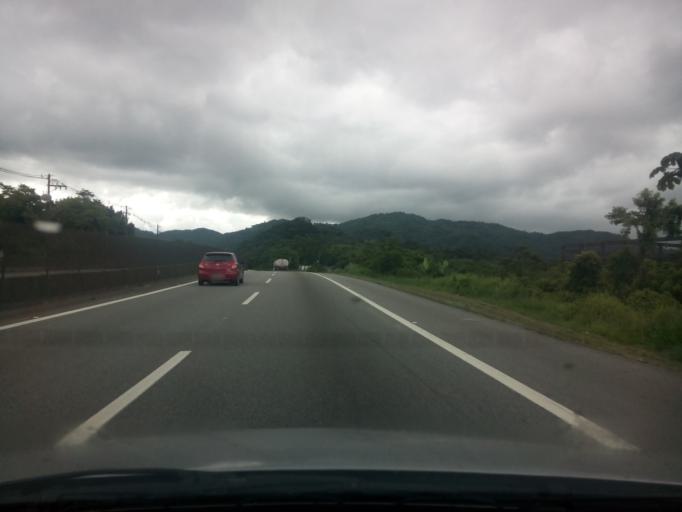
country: BR
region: Sao Paulo
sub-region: Santos
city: Santos
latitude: -23.8901
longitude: -46.3061
